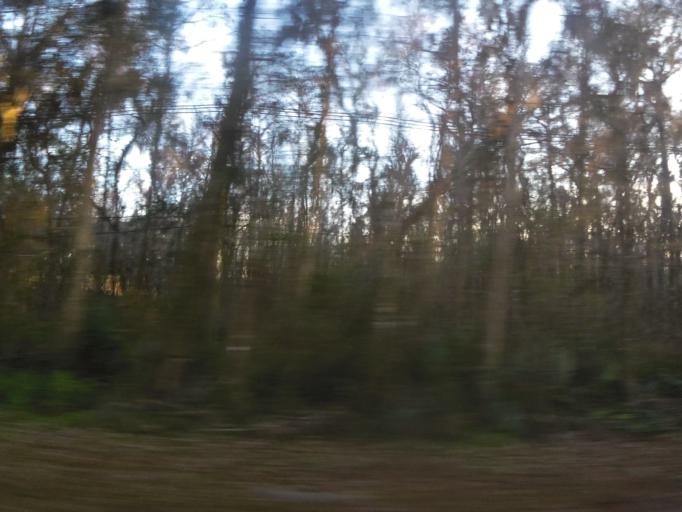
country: US
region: Florida
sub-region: Clay County
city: Green Cove Springs
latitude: 29.9258
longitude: -81.5870
